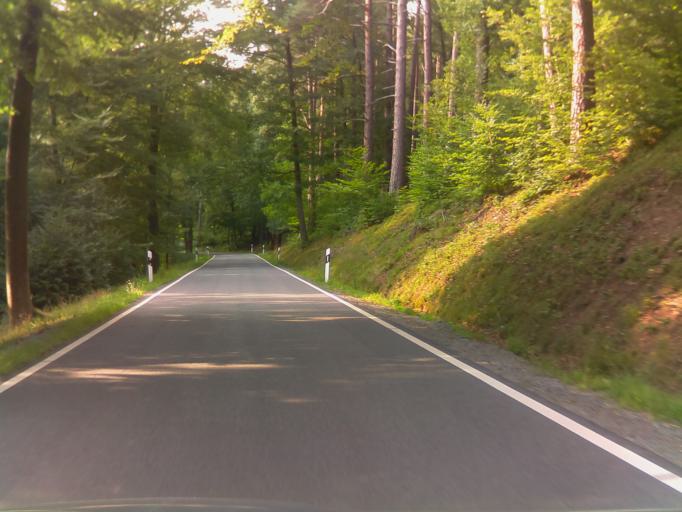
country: DE
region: Hesse
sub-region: Regierungsbezirk Darmstadt
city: Hesseneck
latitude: 49.5660
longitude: 9.0984
